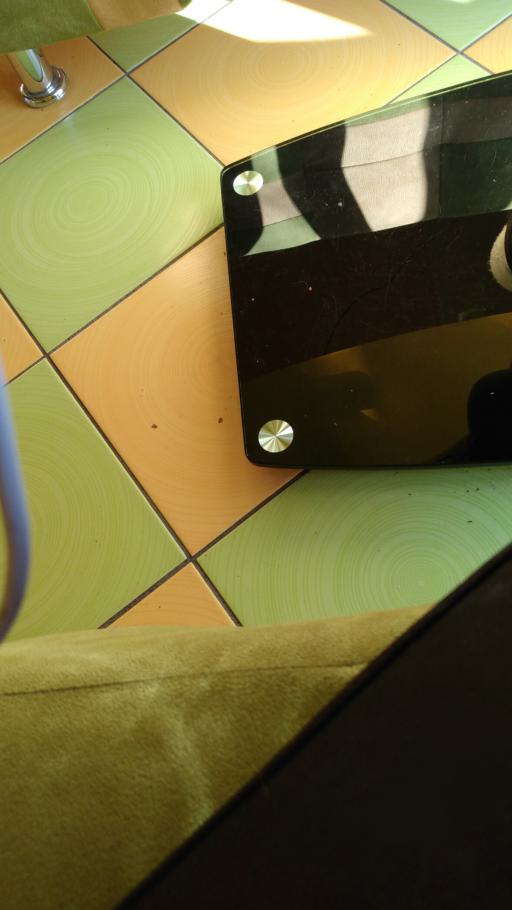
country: RU
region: Tverskaya
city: Kozlovo
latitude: 56.5751
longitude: 36.2799
